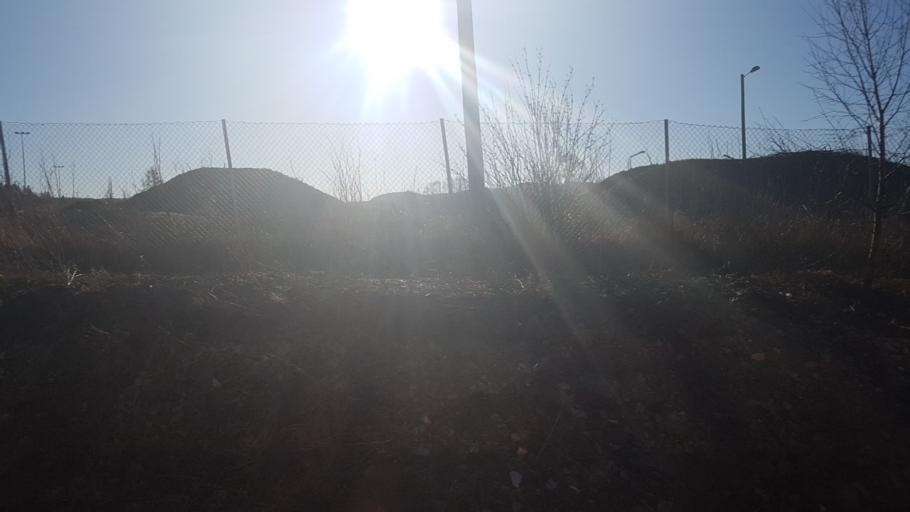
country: NO
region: Nord-Trondelag
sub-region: Levanger
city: Levanger
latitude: 63.7272
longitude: 11.2573
